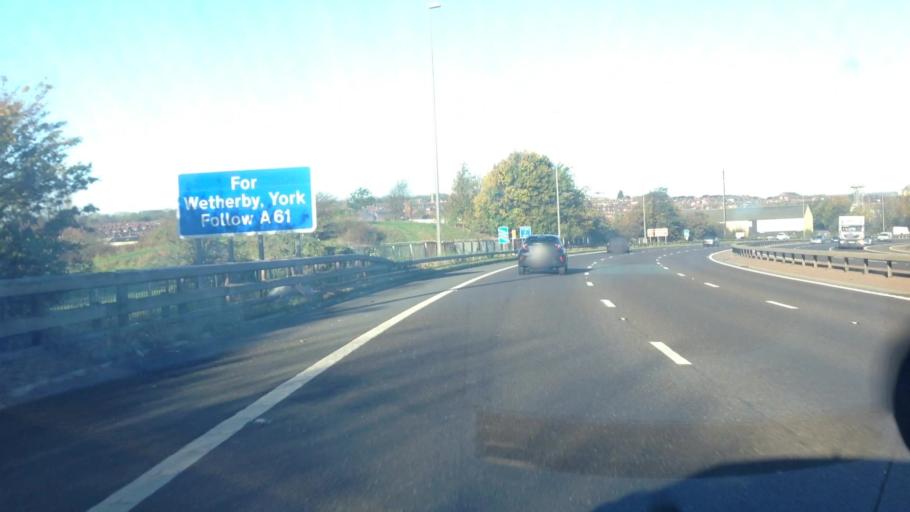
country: GB
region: England
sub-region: City and Borough of Leeds
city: Leeds
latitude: 53.7708
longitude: -1.5376
